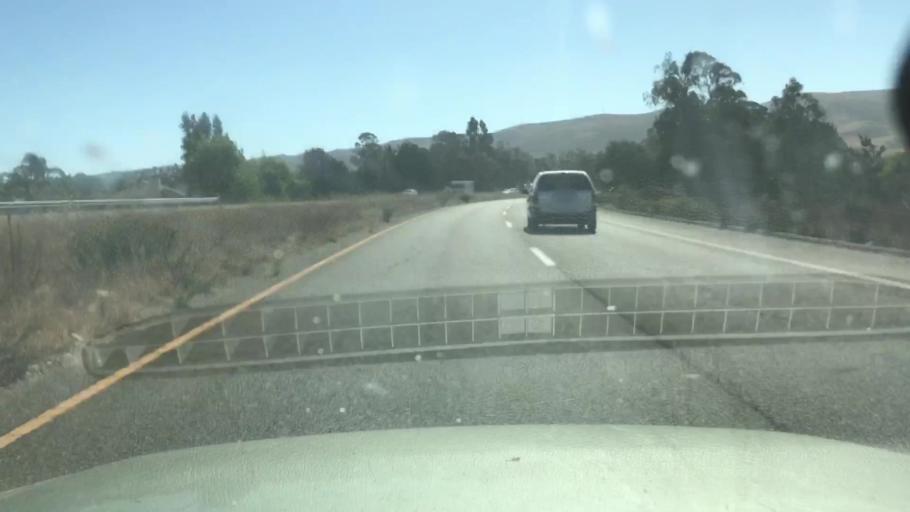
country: US
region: California
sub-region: Santa Barbara County
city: Orcutt
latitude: 34.8609
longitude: -120.4374
